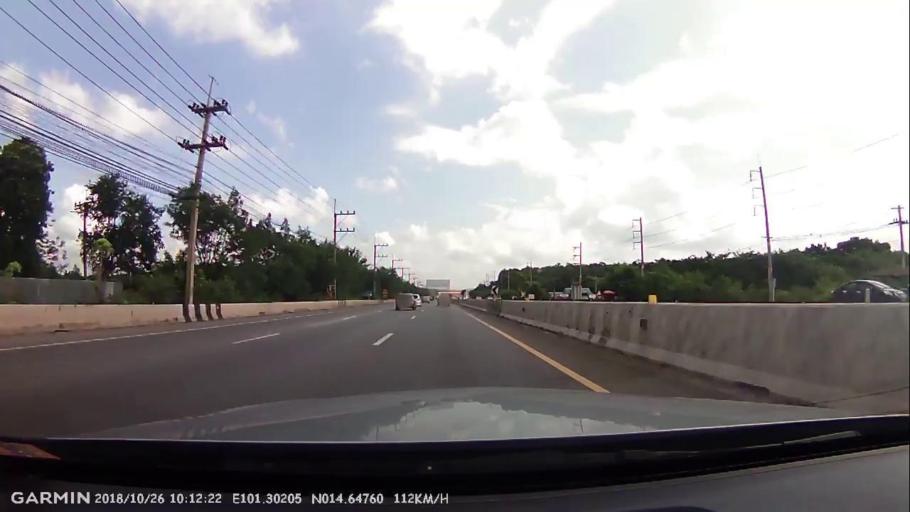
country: TH
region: Sara Buri
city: Muak Lek
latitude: 14.6473
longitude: 101.3023
